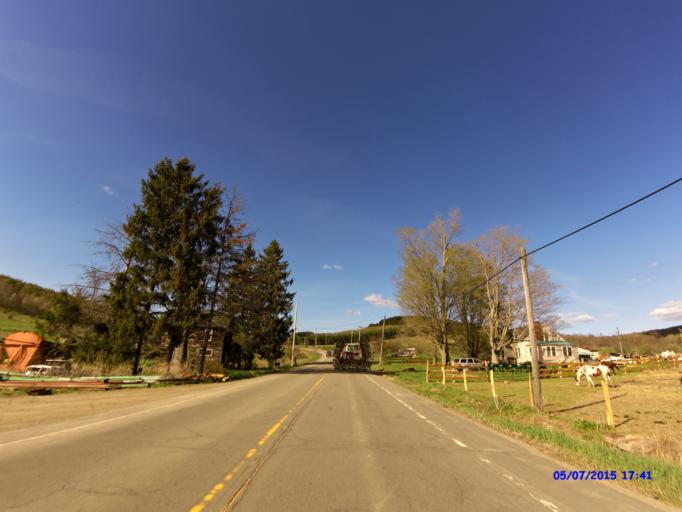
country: US
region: New York
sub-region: Cattaraugus County
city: Franklinville
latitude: 42.2852
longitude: -78.5297
